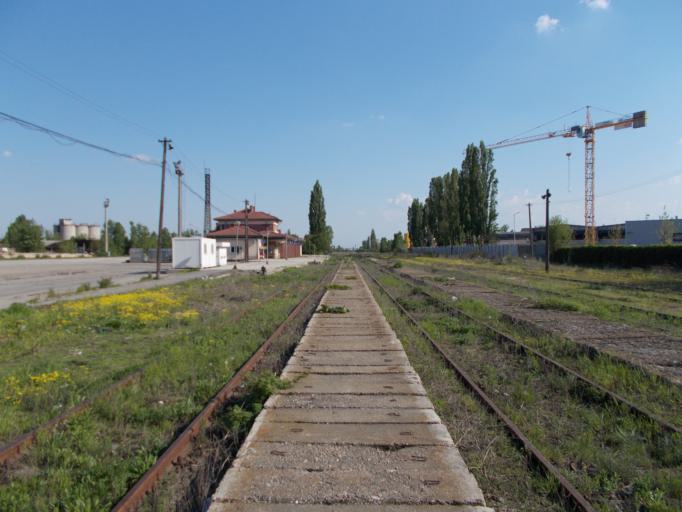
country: RO
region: Ilfov
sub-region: Comuna Jilava
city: Jilava
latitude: 44.3663
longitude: 26.0905
